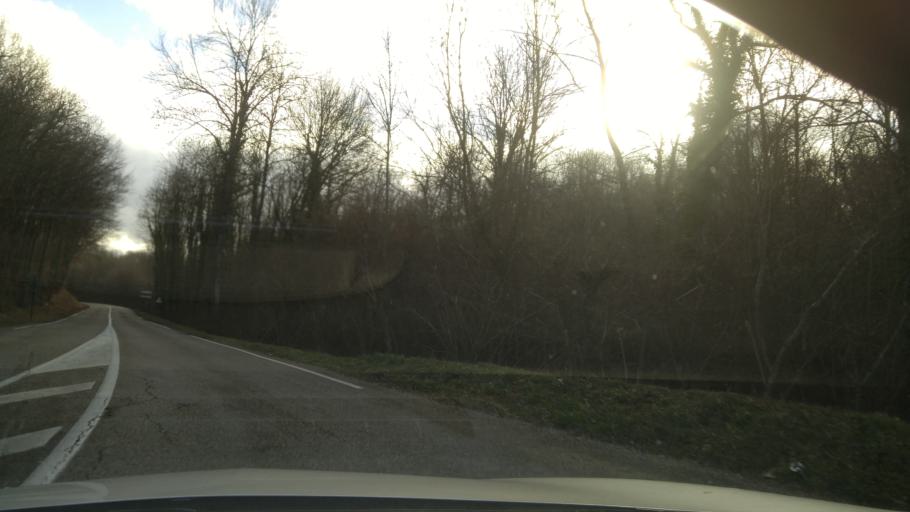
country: FR
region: Rhone-Alpes
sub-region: Departement de l'Isere
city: Roche
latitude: 45.6022
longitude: 5.1596
